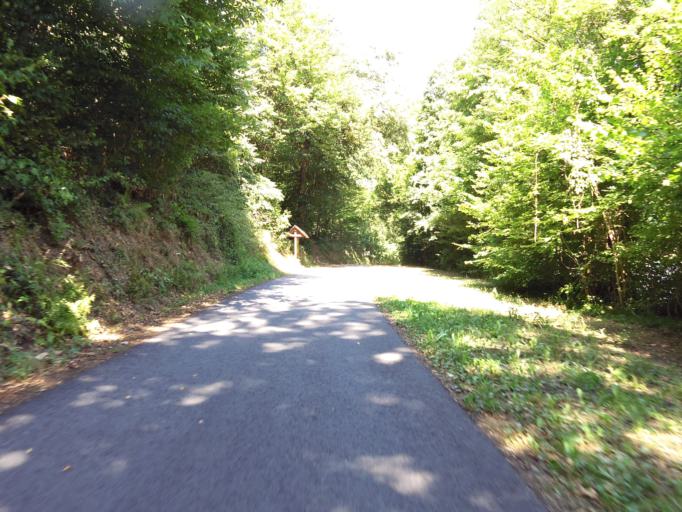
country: DE
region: Baden-Wuerttemberg
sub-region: Karlsruhe Region
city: Zwingenberg
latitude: 49.4266
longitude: 9.0016
